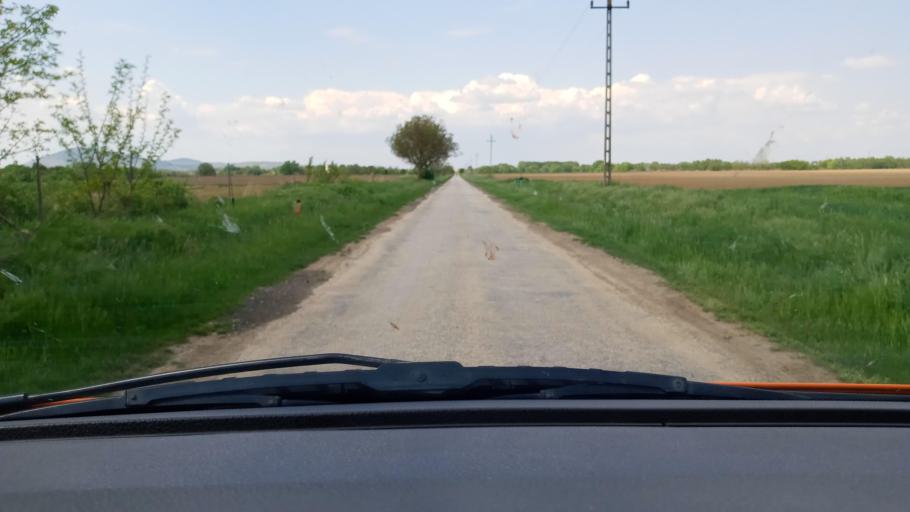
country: HU
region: Baranya
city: Beremend
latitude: 45.8095
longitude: 18.5156
